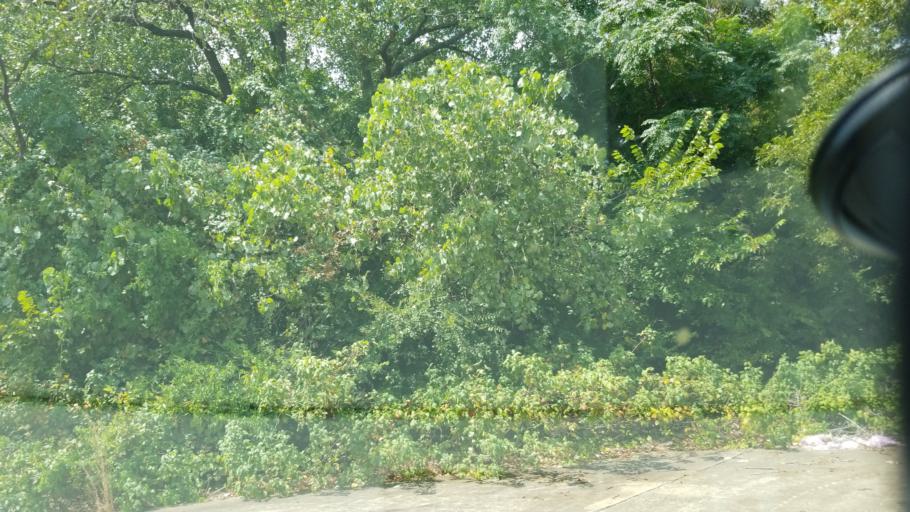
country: US
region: Texas
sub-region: Dallas County
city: Duncanville
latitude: 32.6927
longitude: -96.8948
